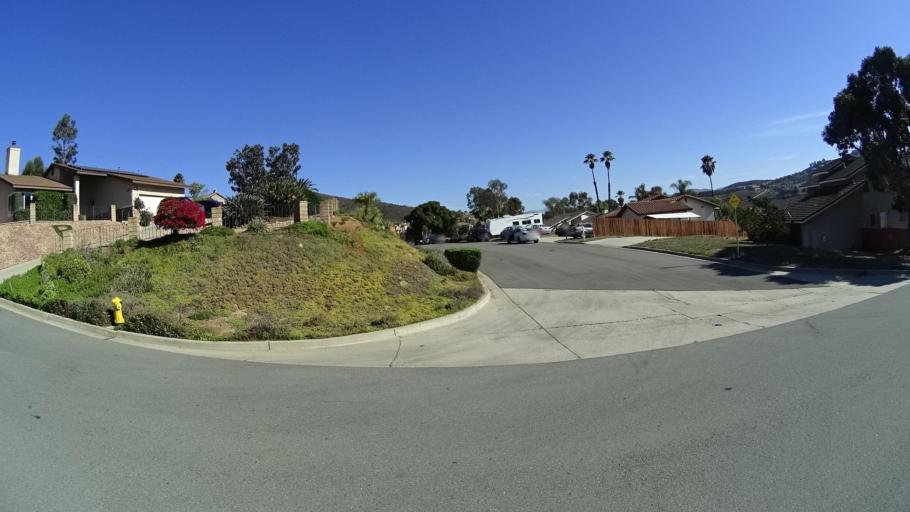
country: US
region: California
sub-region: San Diego County
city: La Presa
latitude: 32.7188
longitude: -116.9812
